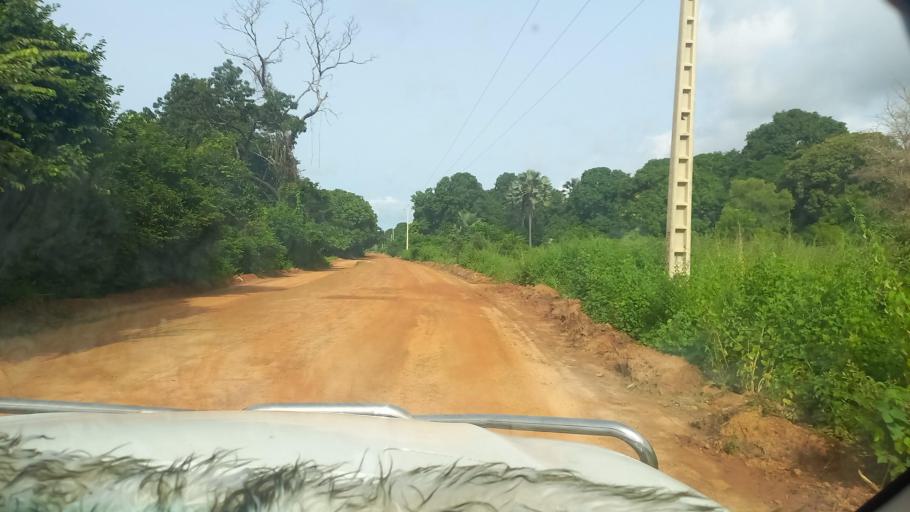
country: SN
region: Ziguinchor
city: Ziguinchor
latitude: 12.6697
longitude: -16.2710
